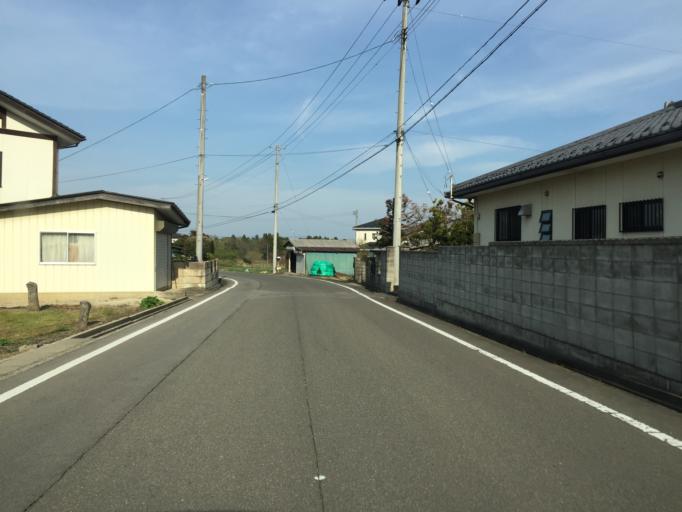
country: JP
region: Fukushima
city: Fukushima-shi
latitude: 37.7650
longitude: 140.3649
